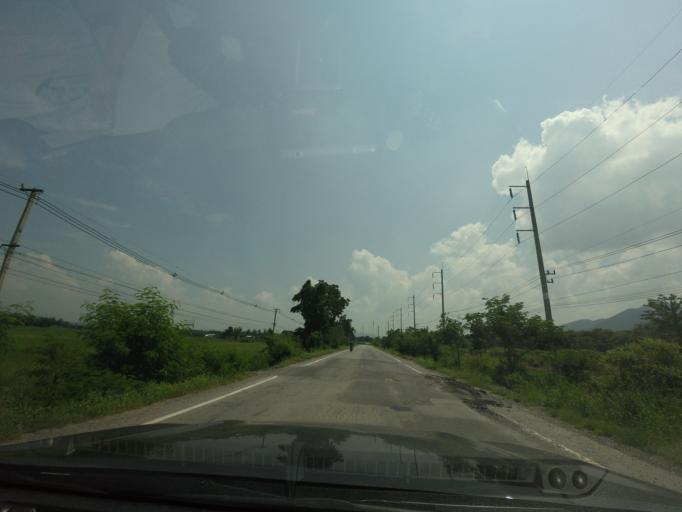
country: TH
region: Uttaradit
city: Thong Saen Khan
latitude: 17.4665
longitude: 100.2701
